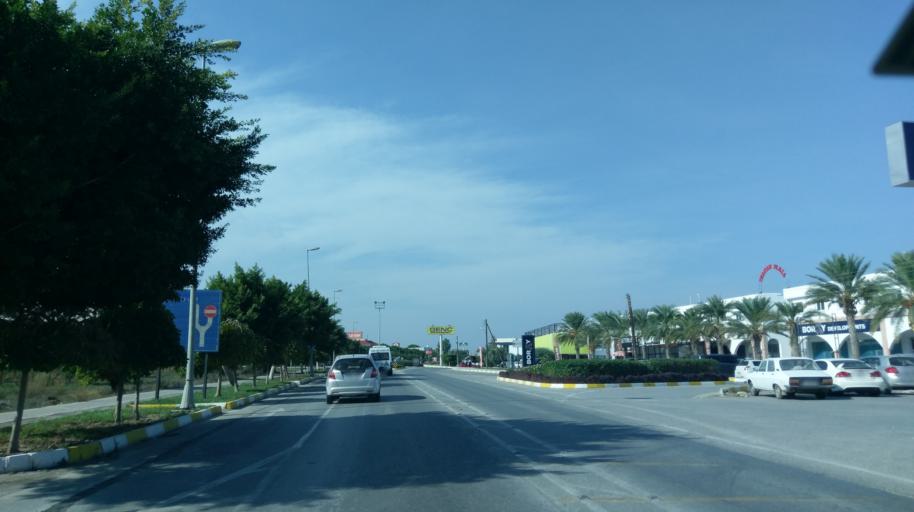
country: CY
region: Keryneia
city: Kyrenia
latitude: 35.3401
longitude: 33.2890
